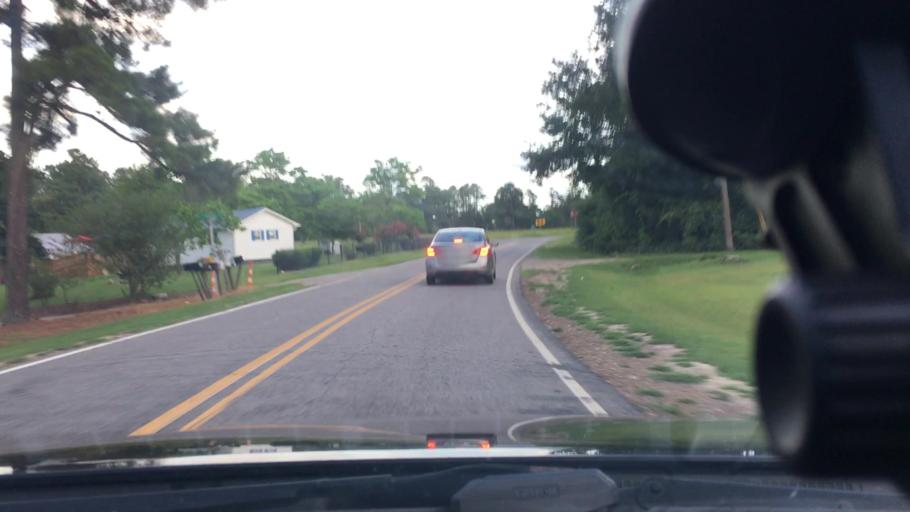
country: US
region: North Carolina
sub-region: Moore County
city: Carthage
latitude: 35.3611
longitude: -79.3268
